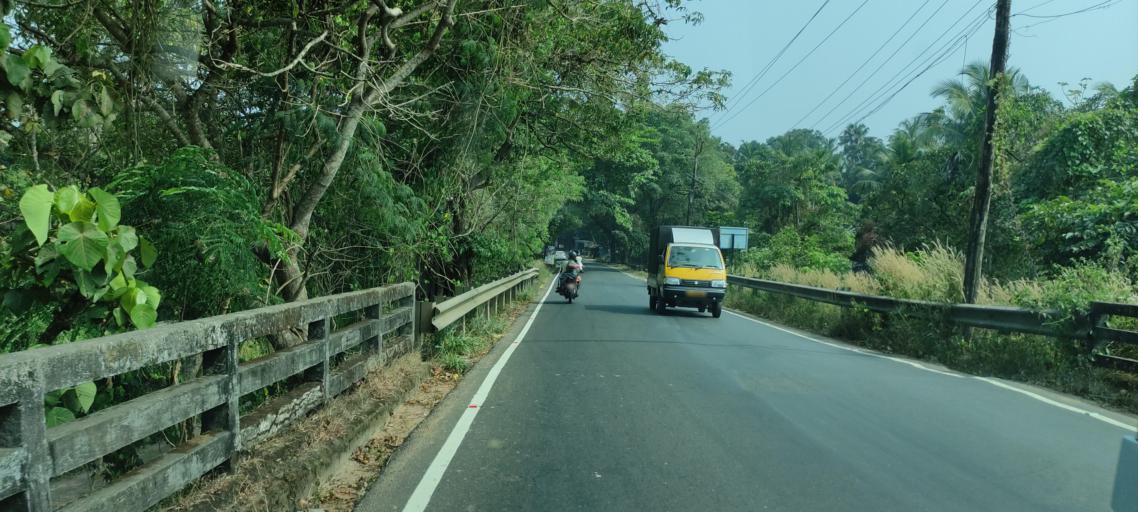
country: IN
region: Kerala
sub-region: Alappuzha
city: Shertallai
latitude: 9.6721
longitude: 76.4060
